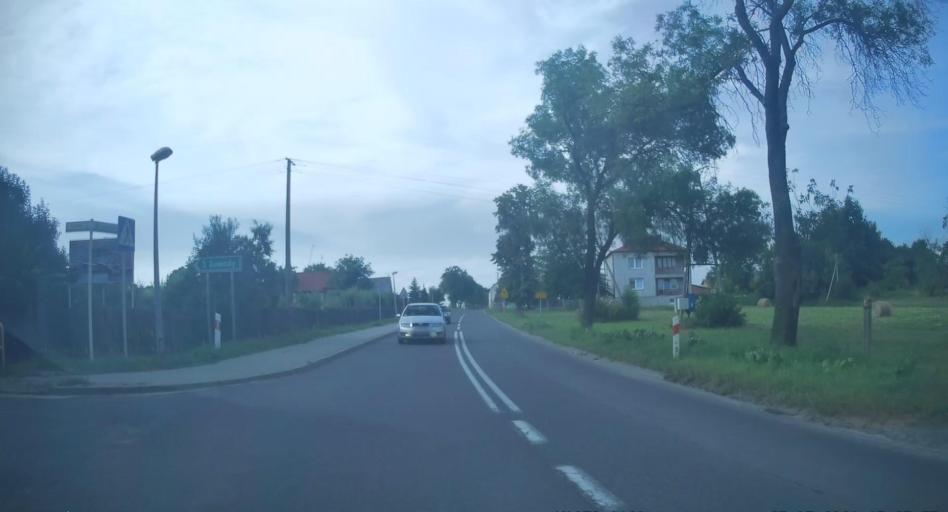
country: PL
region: Lodz Voivodeship
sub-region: Powiat tomaszowski
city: Rzeczyca
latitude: 51.5996
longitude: 20.2940
